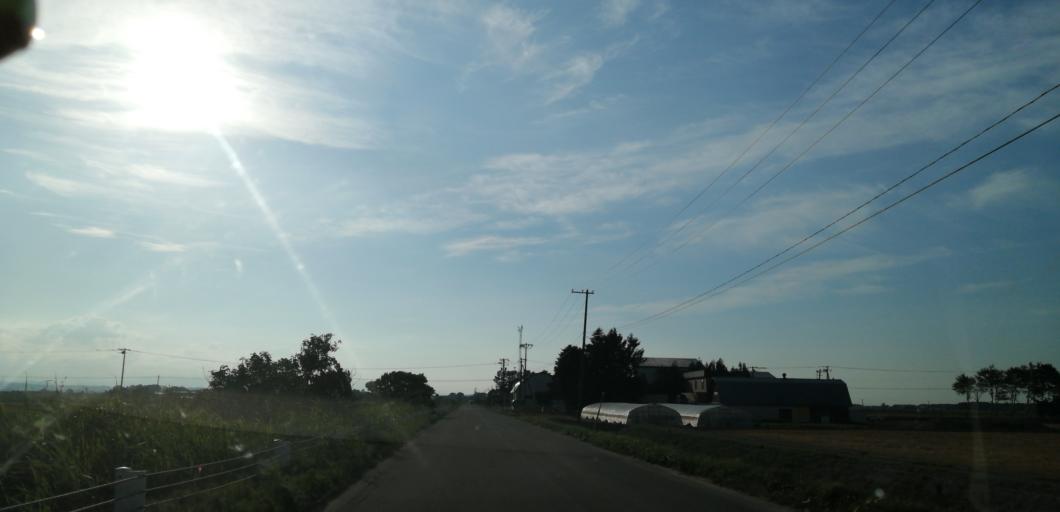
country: JP
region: Hokkaido
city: Kitahiroshima
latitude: 42.9572
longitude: 141.6515
